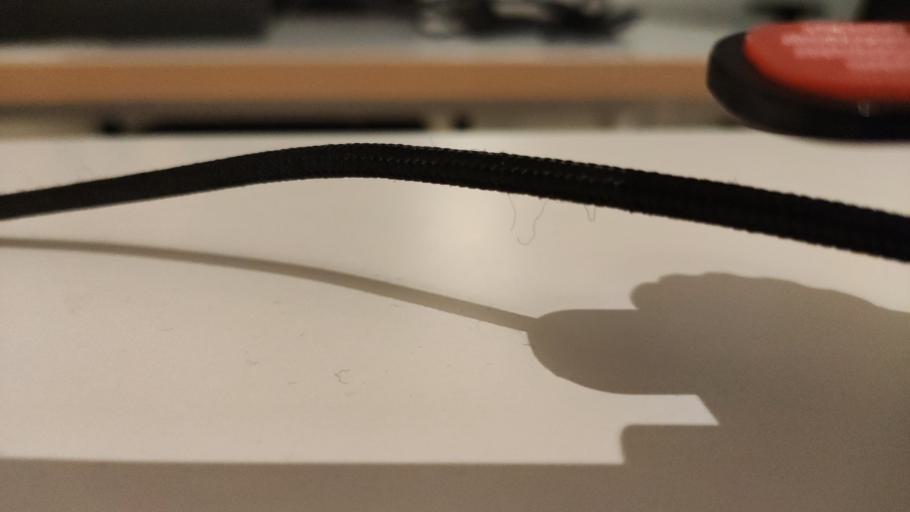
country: RU
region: Moskovskaya
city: Elektrogorsk
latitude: 55.9887
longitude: 38.7808
